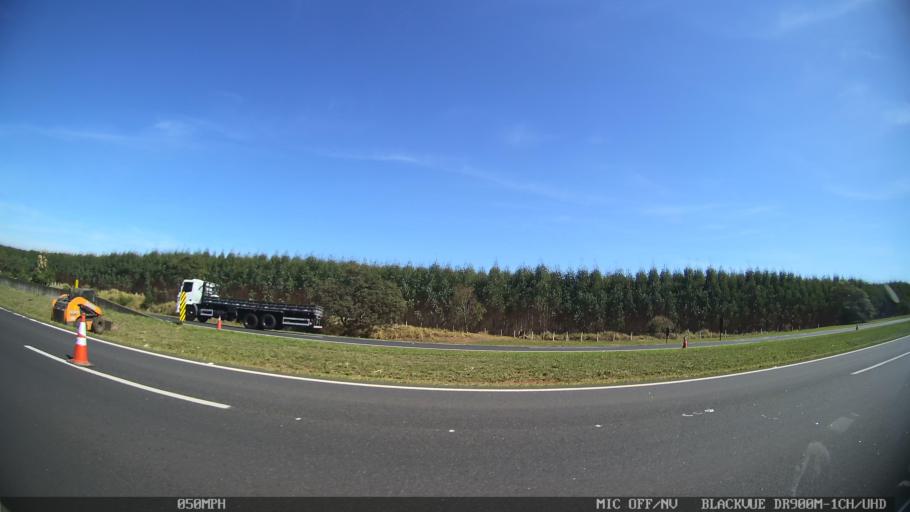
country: BR
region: Sao Paulo
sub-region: Sao Simao
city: Sao Simao
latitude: -21.5670
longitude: -47.6326
